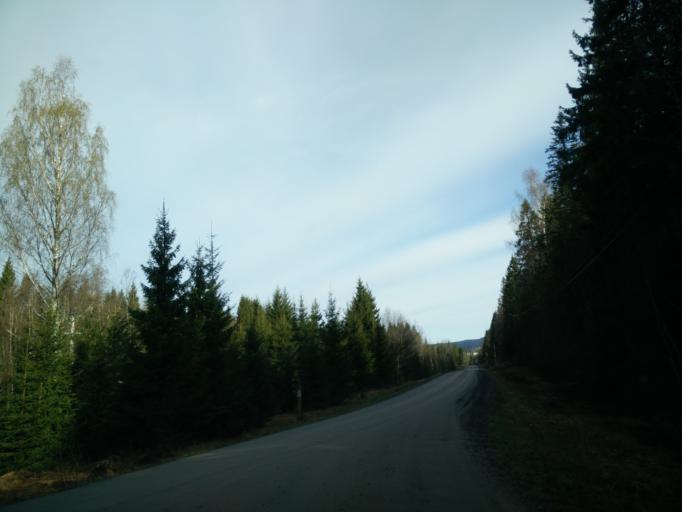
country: SE
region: Vaesternorrland
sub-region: Timra Kommun
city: Soraker
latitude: 62.6295
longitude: 17.6711
